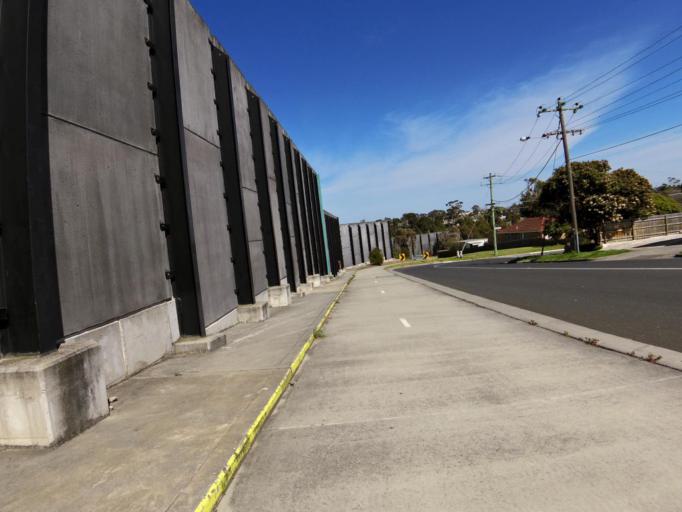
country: AU
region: Victoria
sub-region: Greater Dandenong
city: Dandenong North
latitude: -37.9634
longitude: 145.1965
